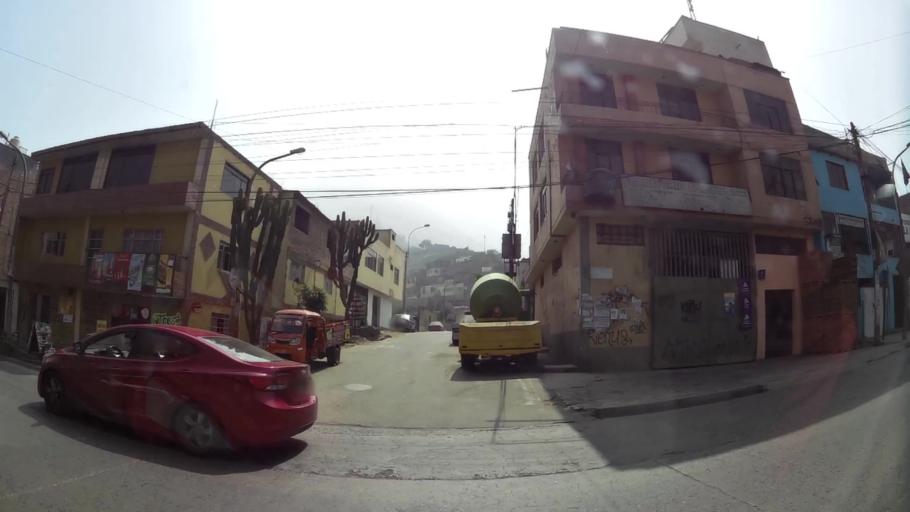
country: PE
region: Lima
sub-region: Lima
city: Chosica
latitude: -11.9423
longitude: -76.7030
